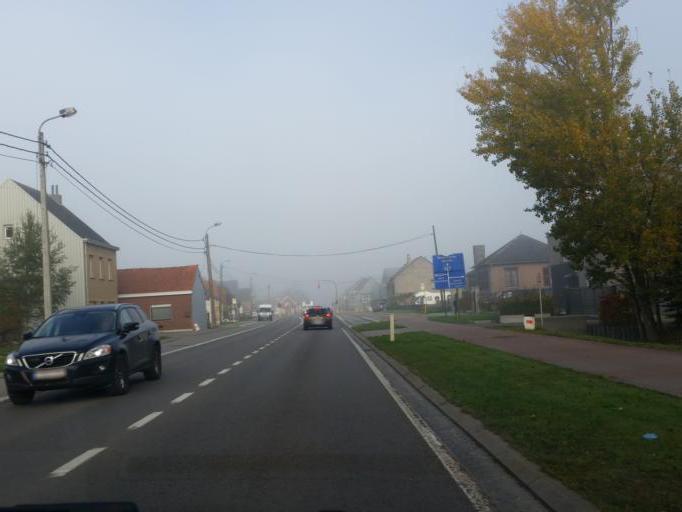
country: BE
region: Flanders
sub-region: Provincie Vlaams-Brabant
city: Opwijk
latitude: 50.9601
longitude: 4.1568
